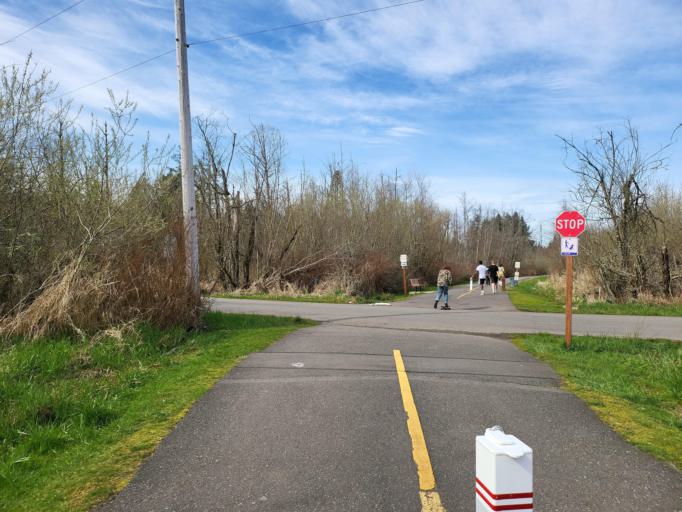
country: US
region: Washington
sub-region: King County
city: East Hill-Meridian
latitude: 47.4085
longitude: -122.1593
